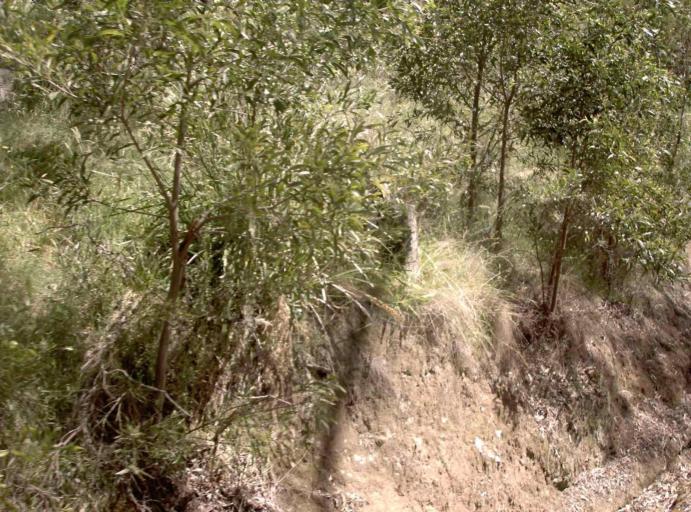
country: AU
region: Victoria
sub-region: East Gippsland
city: Lakes Entrance
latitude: -37.2256
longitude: 148.2637
